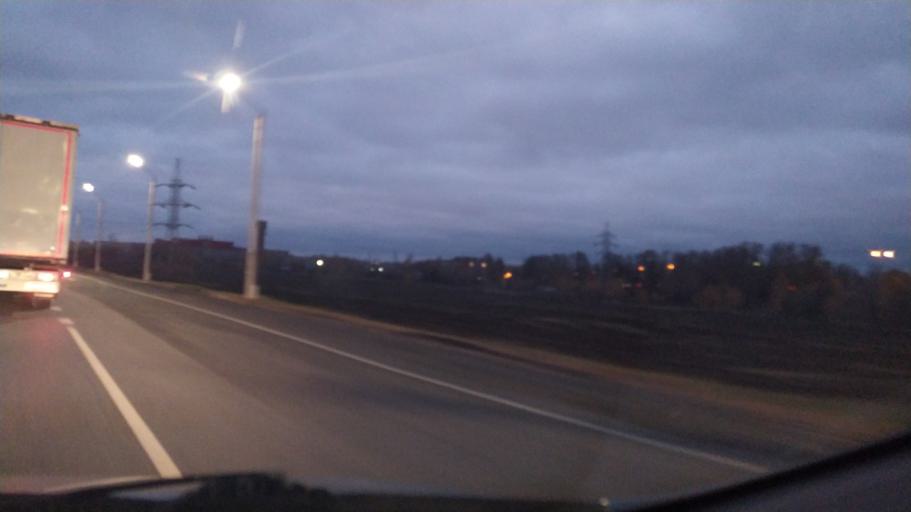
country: RU
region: Chuvashia
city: Kugesi
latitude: 56.0496
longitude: 47.2842
